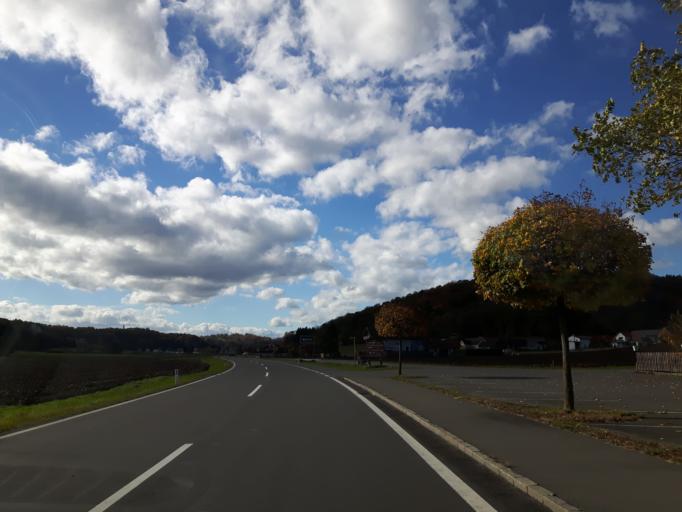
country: AT
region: Styria
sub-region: Politischer Bezirk Suedoststeiermark
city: Paldau
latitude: 46.9500
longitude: 15.8179
